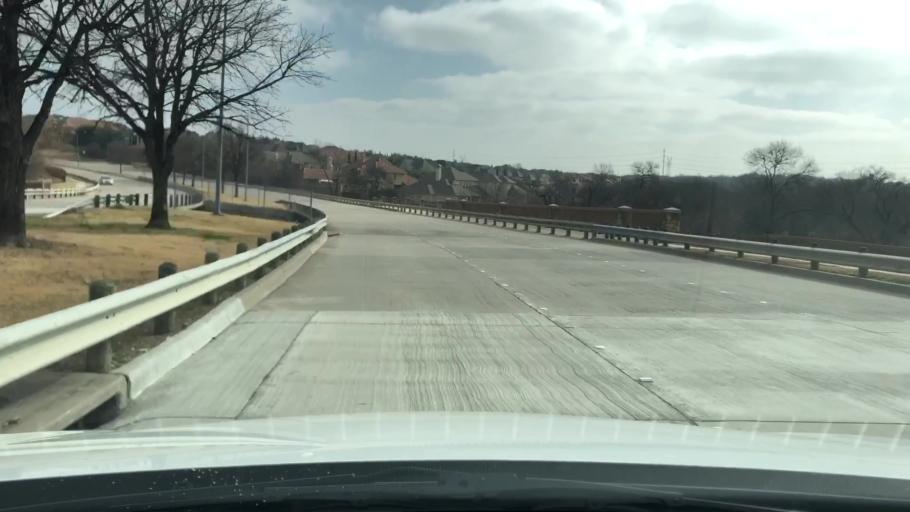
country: US
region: Texas
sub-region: Denton County
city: The Colony
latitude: 33.0705
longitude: -96.8501
